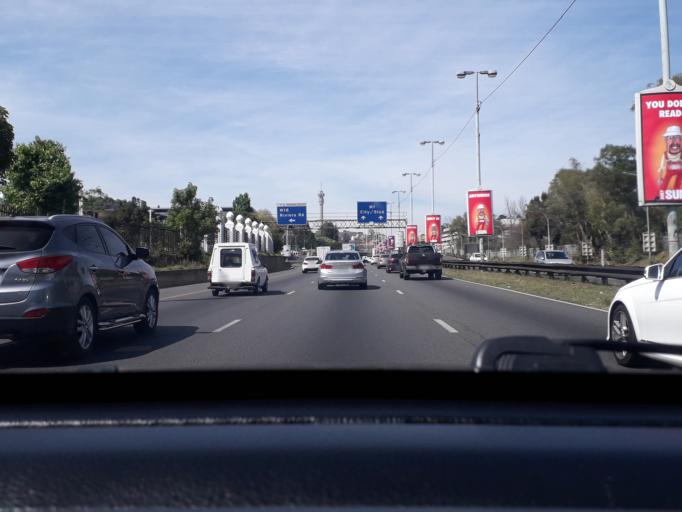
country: ZA
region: Gauteng
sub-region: City of Johannesburg Metropolitan Municipality
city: Johannesburg
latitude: -26.1621
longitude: 28.0571
